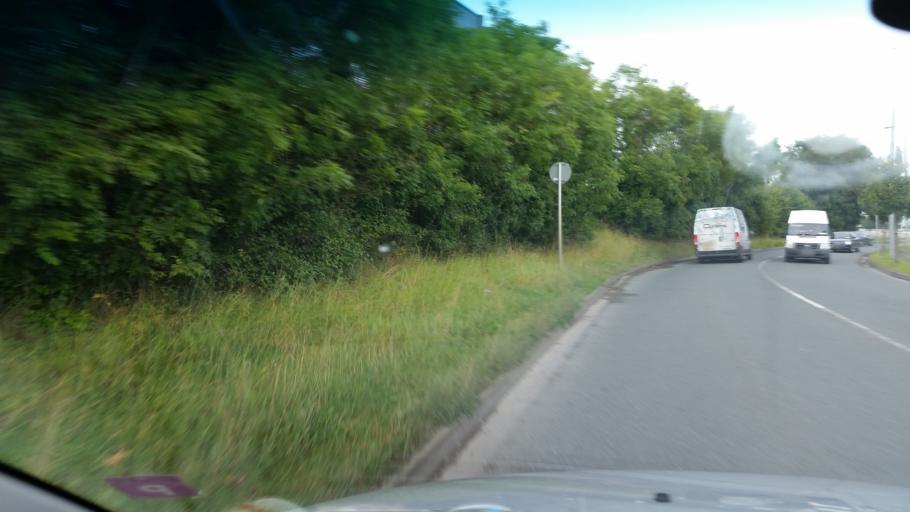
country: IE
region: Leinster
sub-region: Fingal County
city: Blanchardstown
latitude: 53.4145
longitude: -6.3557
